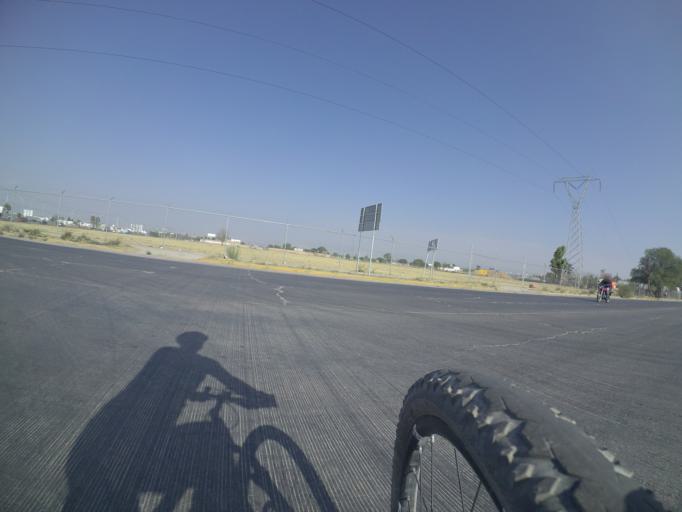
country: MX
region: Aguascalientes
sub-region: Jesus Maria
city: Arboledas Paso Blanco [Fraccionamiento]
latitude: 21.9465
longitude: -102.2970
